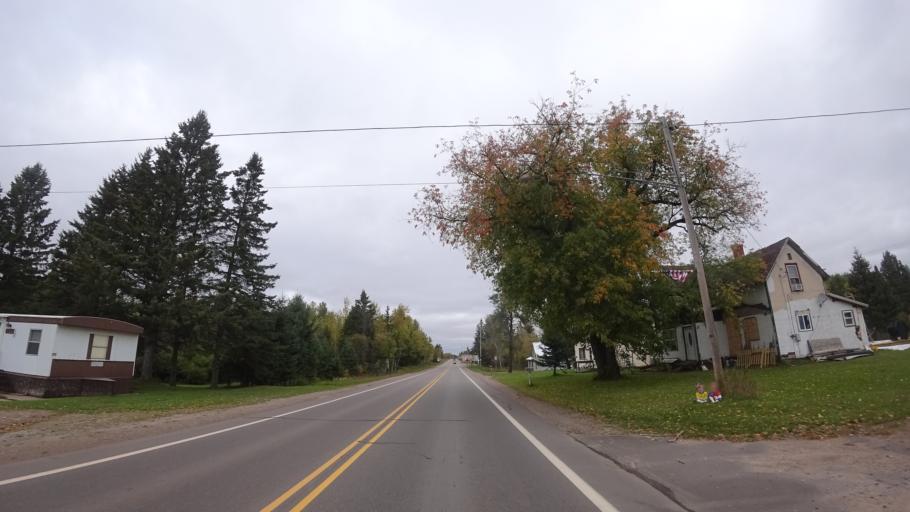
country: US
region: Michigan
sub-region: Iron County
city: Crystal Falls
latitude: 46.1366
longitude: -88.0931
